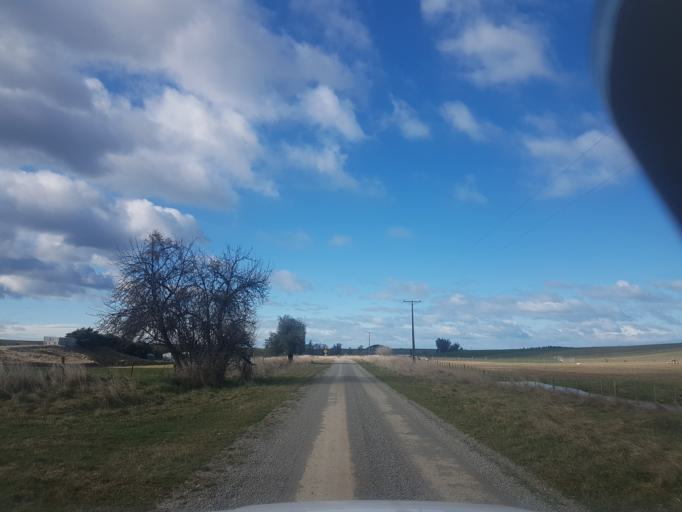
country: NZ
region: Canterbury
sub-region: Timaru District
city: Pleasant Point
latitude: -44.1887
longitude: 171.1792
